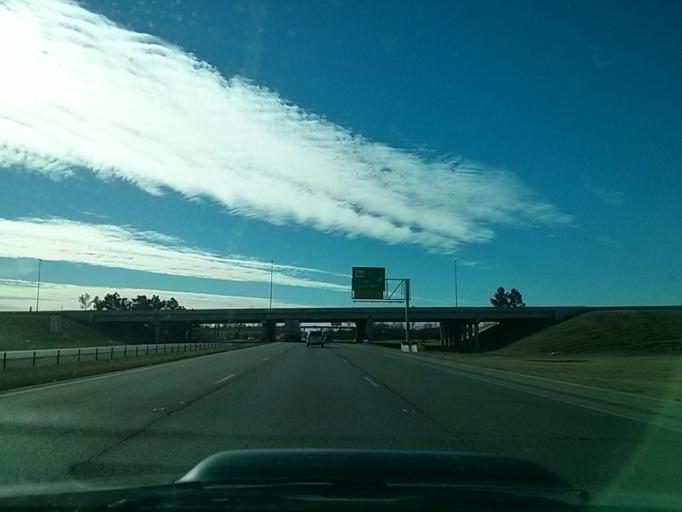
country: US
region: Oklahoma
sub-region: Tulsa County
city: Jenks
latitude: 36.0114
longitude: -96.0117
